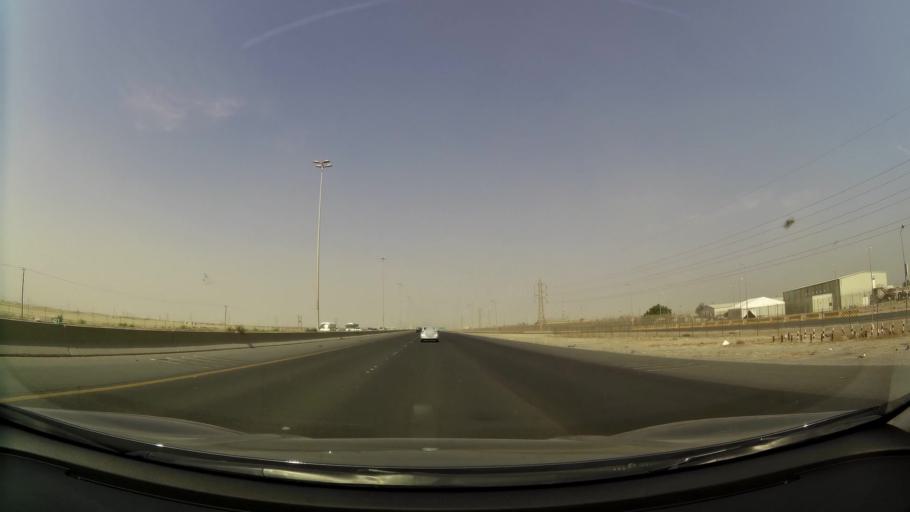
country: KW
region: Al Ahmadi
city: Al Fahahil
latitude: 29.0250
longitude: 48.1250
